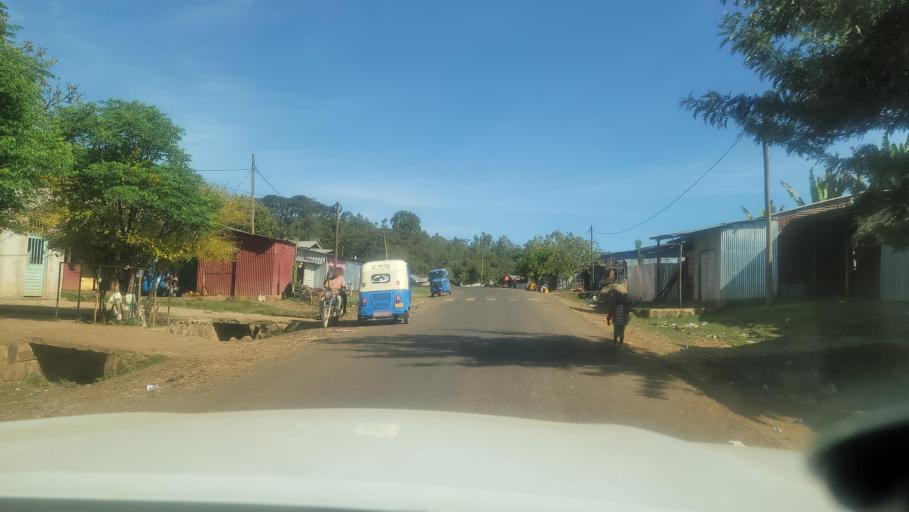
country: ET
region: Oromiya
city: Agaro
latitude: 7.7974
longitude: 36.4774
